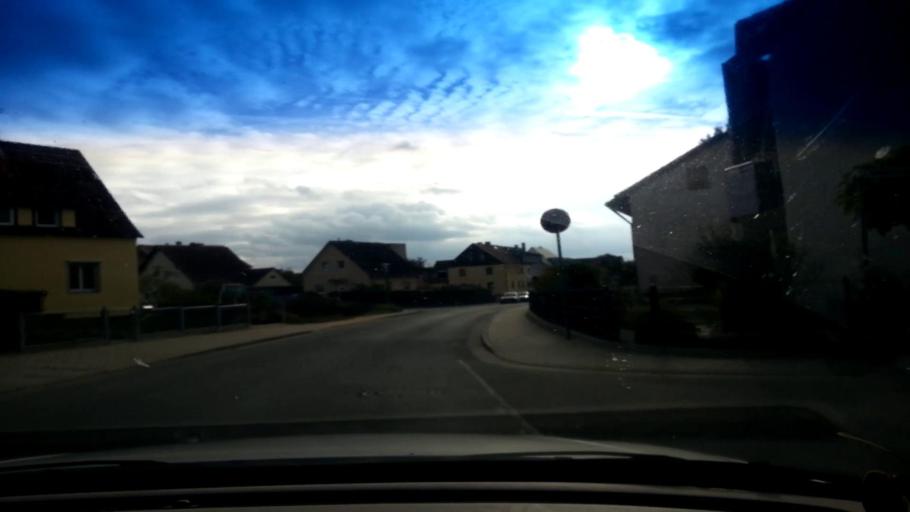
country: DE
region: Bavaria
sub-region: Upper Franconia
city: Hallstadt
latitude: 49.9262
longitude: 10.8823
